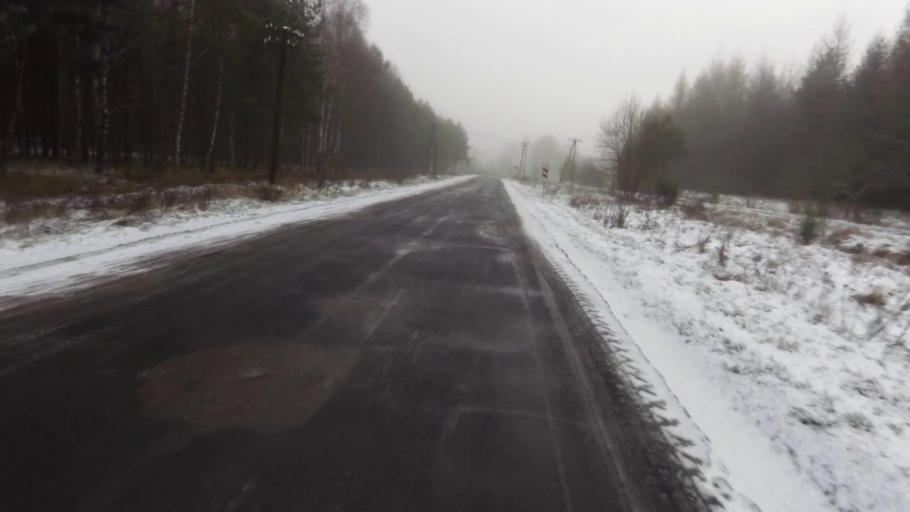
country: PL
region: West Pomeranian Voivodeship
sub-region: Powiat drawski
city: Wierzchowo
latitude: 53.4457
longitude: 16.1546
